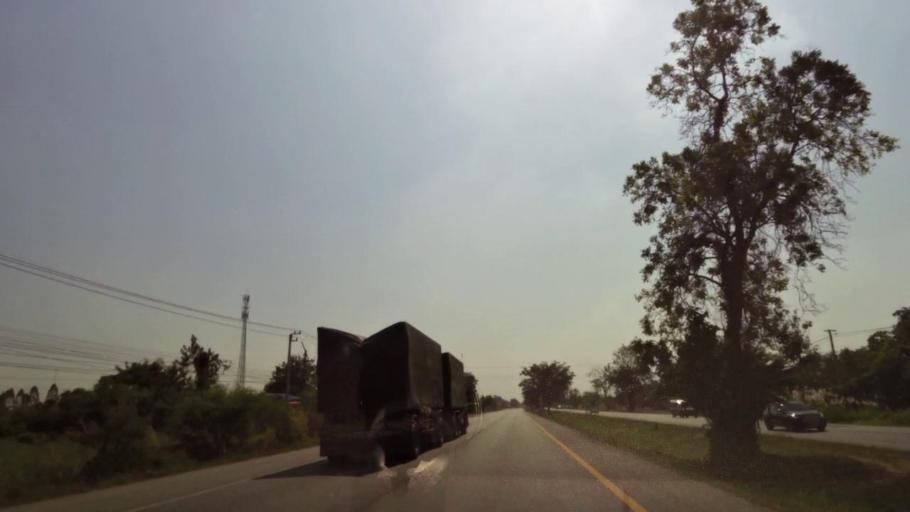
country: TH
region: Phichit
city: Bueng Na Rang
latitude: 16.3090
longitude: 100.1286
